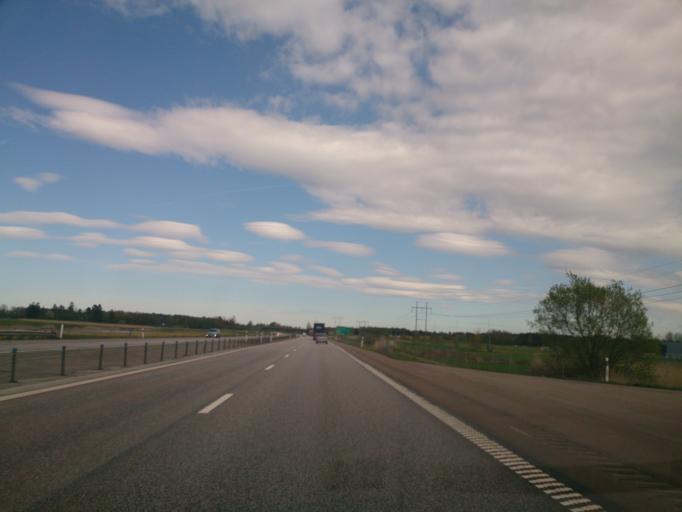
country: SE
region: OEstergoetland
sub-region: Linkopings Kommun
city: Linkoping
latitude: 58.4324
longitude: 15.6565
